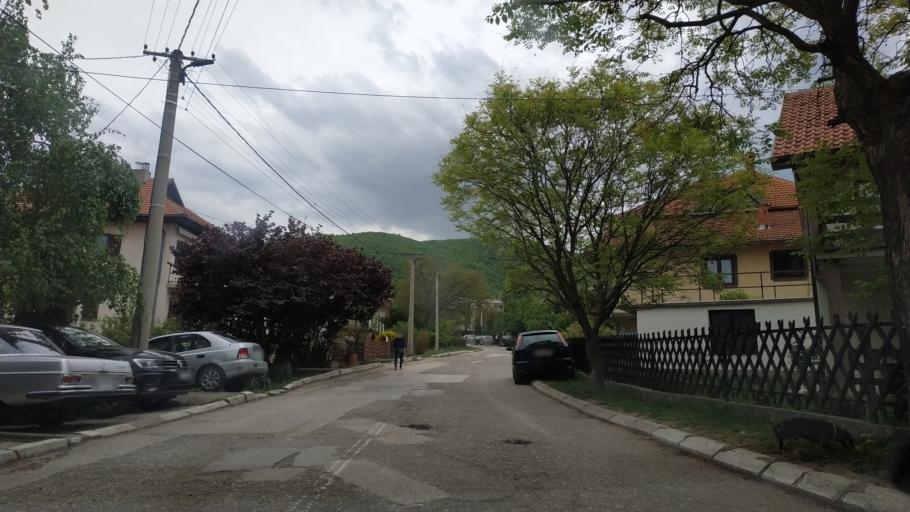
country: RS
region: Central Serbia
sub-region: Zajecarski Okrug
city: Soko Banja
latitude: 43.6427
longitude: 21.8655
